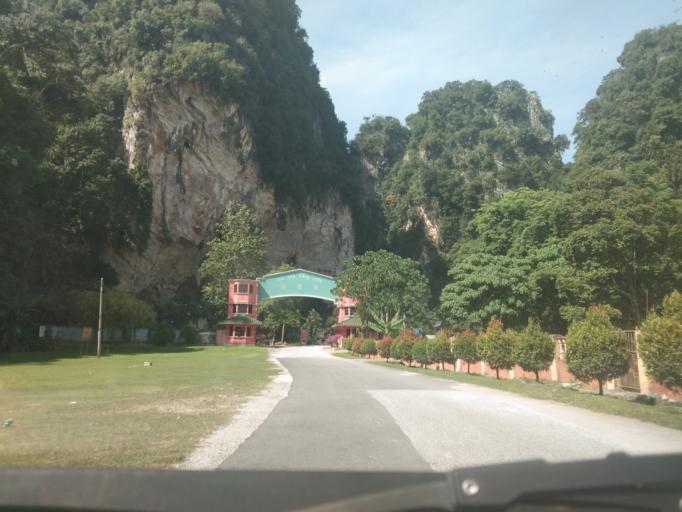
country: MY
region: Perak
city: Ipoh
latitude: 4.5599
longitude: 101.1295
